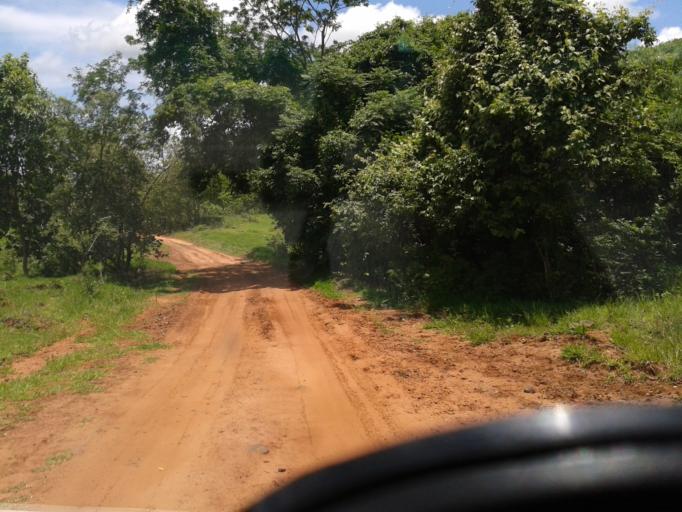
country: BR
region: Minas Gerais
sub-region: Santa Vitoria
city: Santa Vitoria
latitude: -18.9872
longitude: -49.8998
